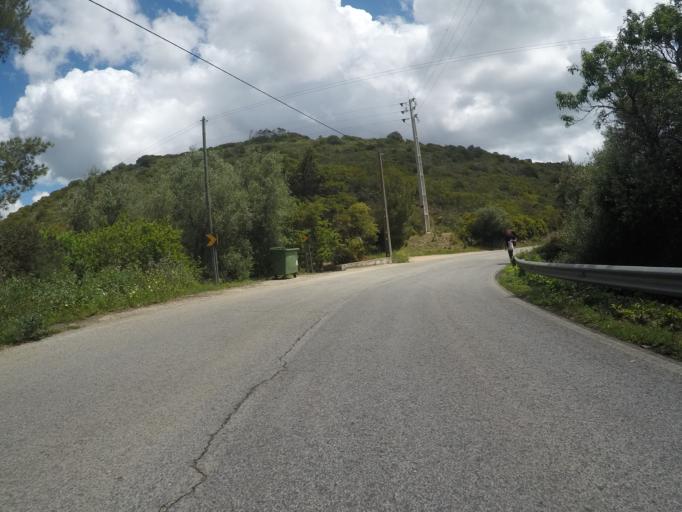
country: PT
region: Faro
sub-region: Vila do Bispo
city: Vila do Bispo
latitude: 37.0721
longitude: -8.8280
